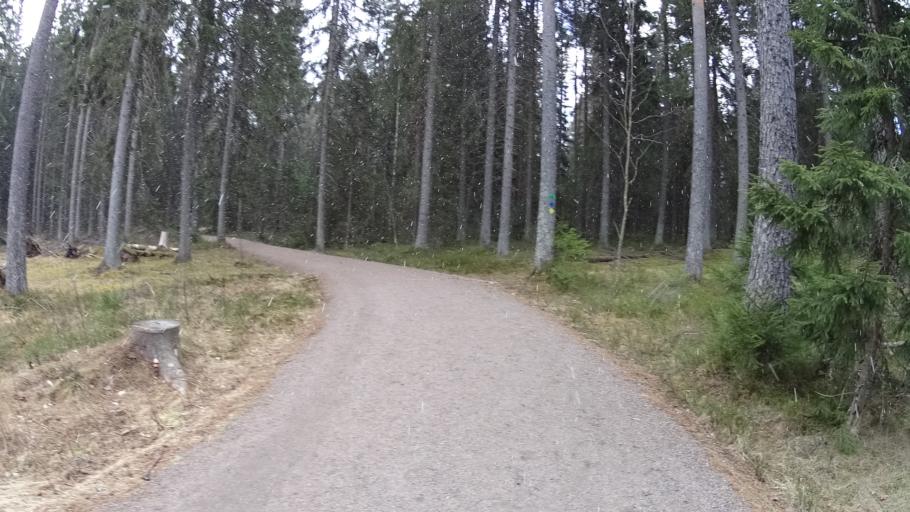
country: FI
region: Uusimaa
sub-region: Helsinki
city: Espoo
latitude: 60.2679
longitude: 24.6322
